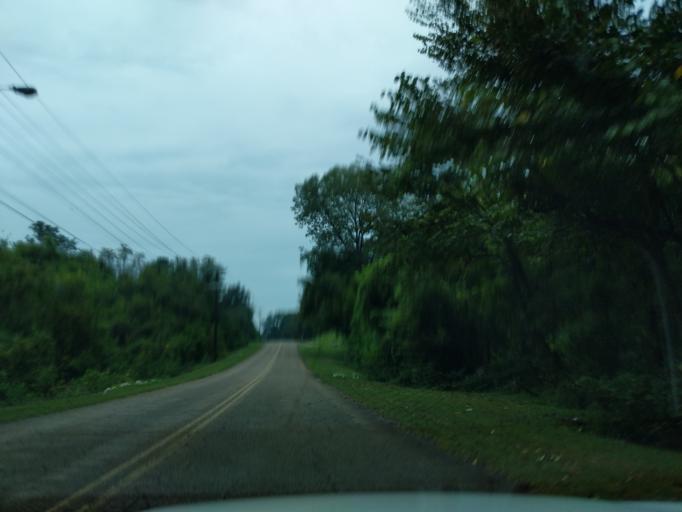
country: US
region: Mississippi
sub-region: Warren County
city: Vicksburg
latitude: 32.3169
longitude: -90.8862
